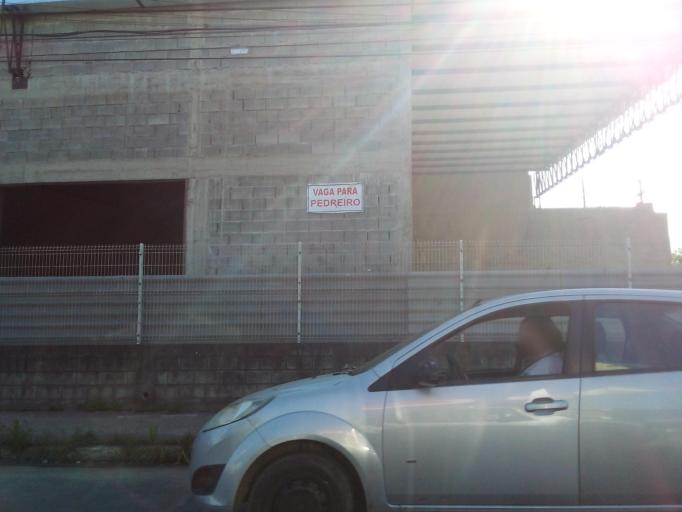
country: BR
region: Espirito Santo
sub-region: Vitoria
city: Vitoria
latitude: -20.3110
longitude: -40.3698
